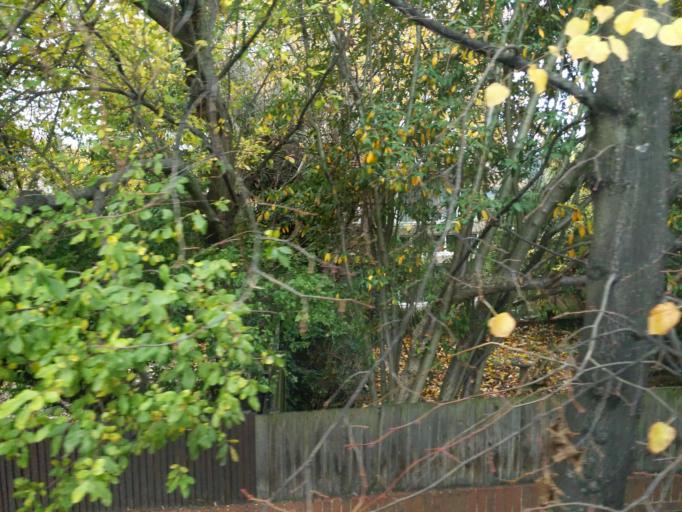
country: GB
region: England
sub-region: Greater London
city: Hammersmith
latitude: 51.4971
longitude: -0.2492
